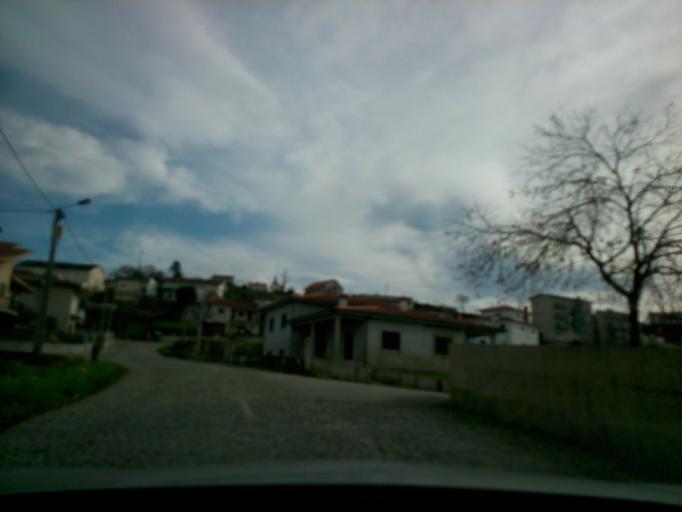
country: PT
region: Porto
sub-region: Amarante
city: Figueiro
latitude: 41.2936
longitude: -8.2104
